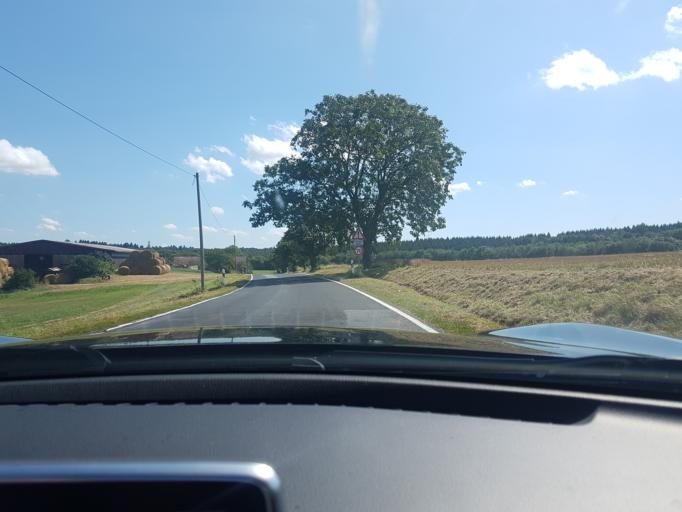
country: DE
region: Baden-Wuerttemberg
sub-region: Karlsruhe Region
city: Billigheim
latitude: 49.3340
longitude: 9.2709
